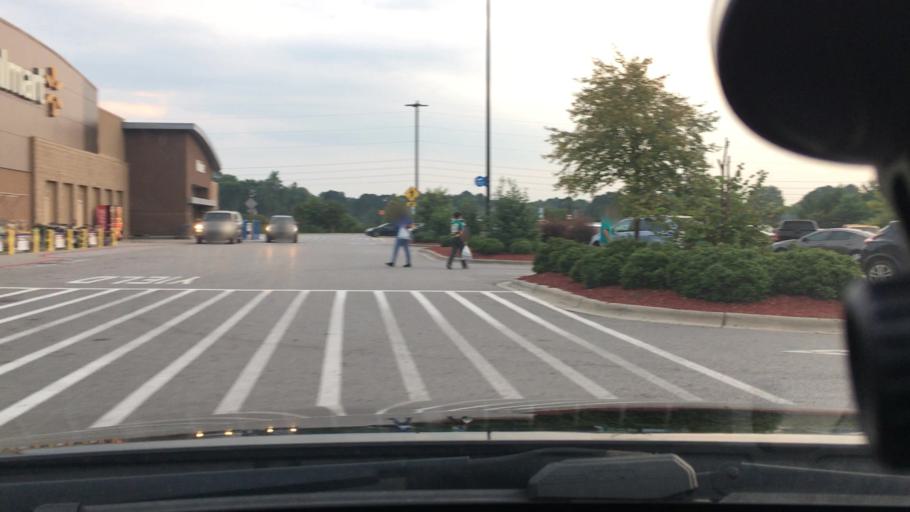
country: US
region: North Carolina
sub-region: Pitt County
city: Windsor
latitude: 35.5808
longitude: -77.3067
